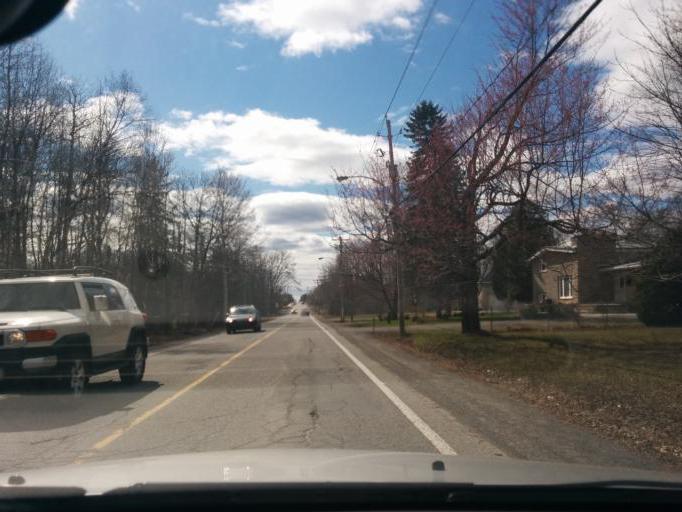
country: CA
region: Ontario
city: Ottawa
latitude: 45.4137
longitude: -75.7900
